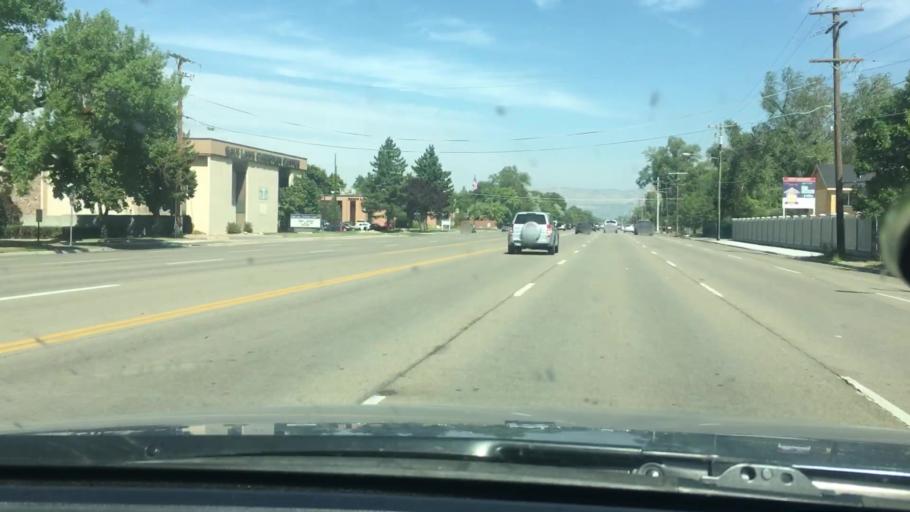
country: US
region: Utah
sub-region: Salt Lake County
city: Millcreek
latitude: 40.6774
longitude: -111.8714
